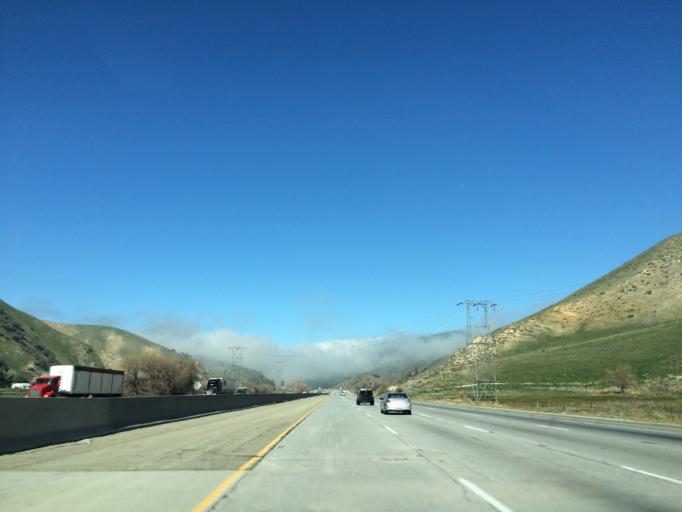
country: US
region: California
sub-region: Kern County
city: Lebec
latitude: 34.8520
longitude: -118.8720
